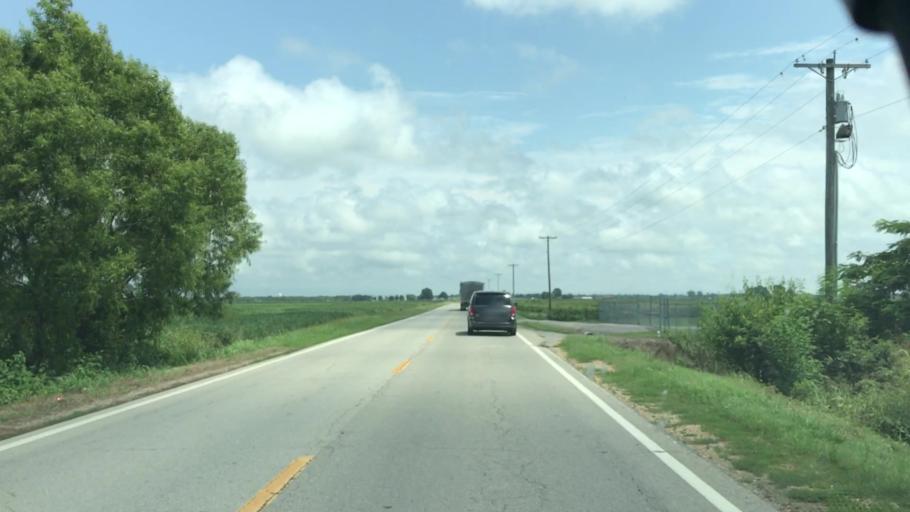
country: US
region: Missouri
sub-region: Pemiscot County
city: Caruthersville
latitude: 36.1760
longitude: -89.7179
